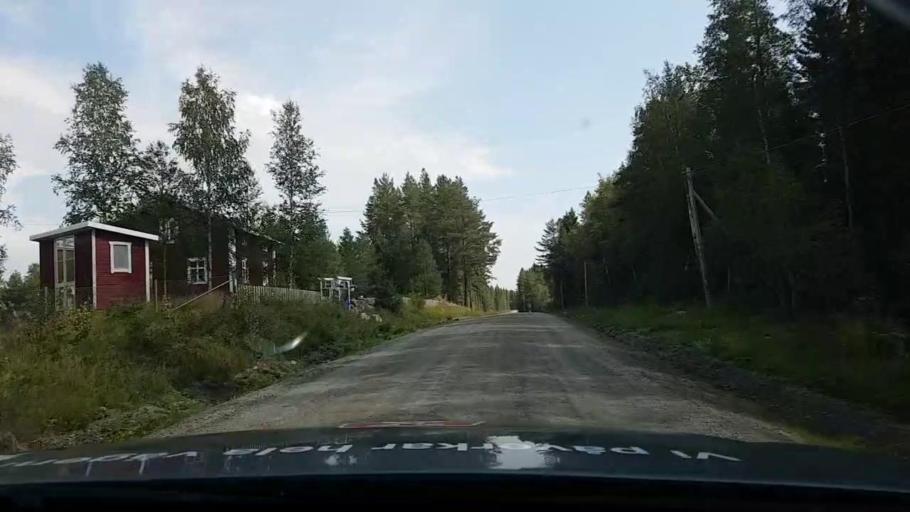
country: SE
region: Jaemtland
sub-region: Braecke Kommun
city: Braecke
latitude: 62.7286
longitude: 15.4915
